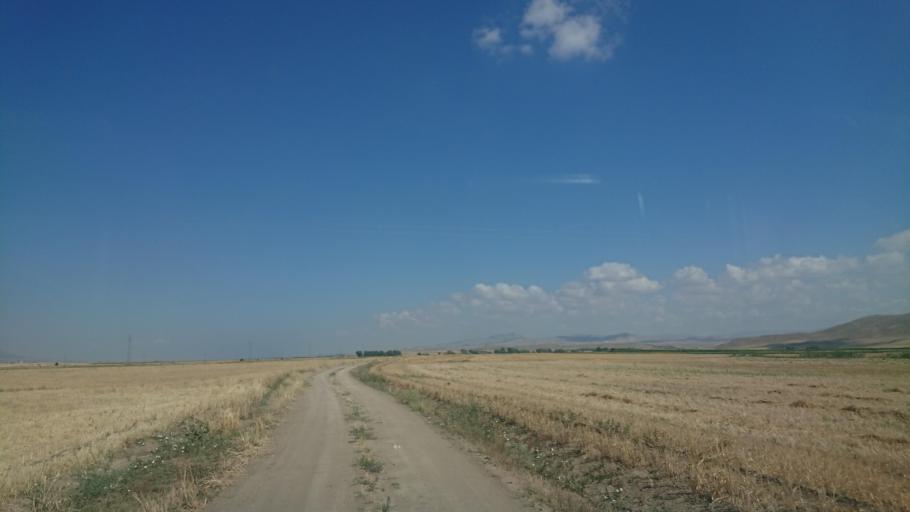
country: TR
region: Aksaray
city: Sariyahsi
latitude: 38.9860
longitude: 33.9038
